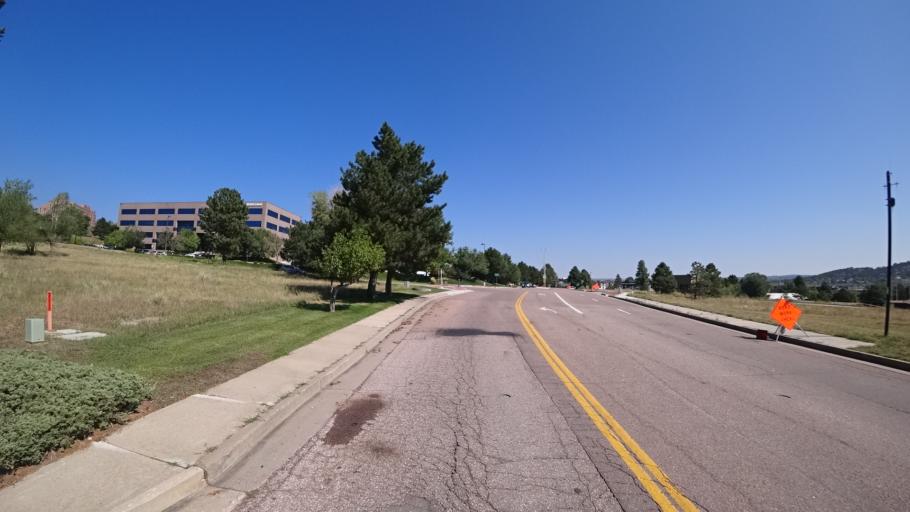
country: US
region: Colorado
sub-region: El Paso County
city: Colorado Springs
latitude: 38.9111
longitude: -104.8258
